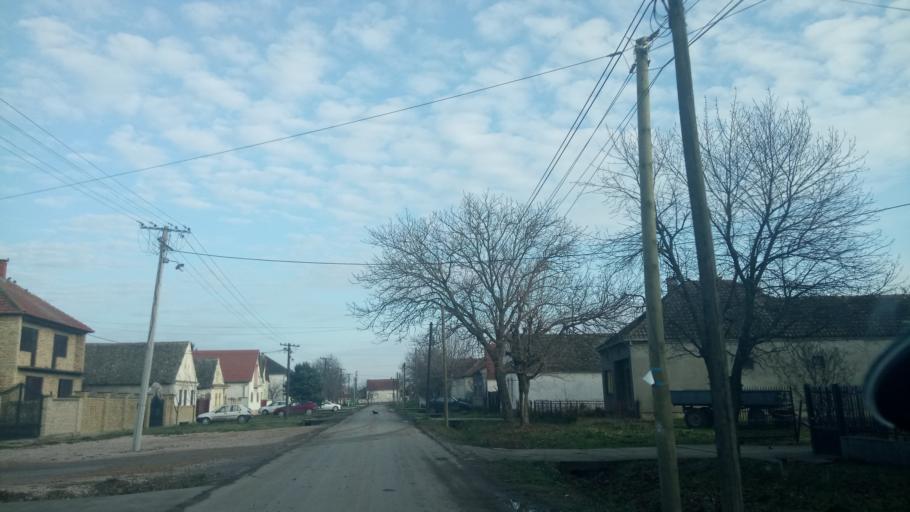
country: RS
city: Vojka
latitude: 44.9318
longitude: 20.1426
